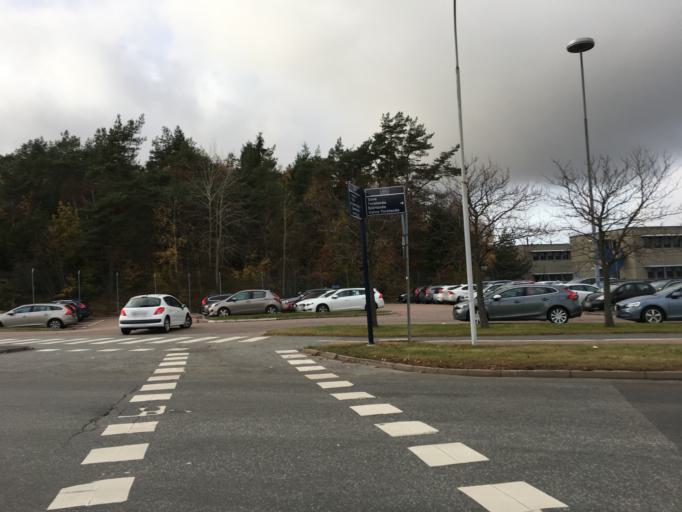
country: SE
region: Vaestra Goetaland
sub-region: Goteborg
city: Majorna
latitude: 57.7274
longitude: 11.8590
